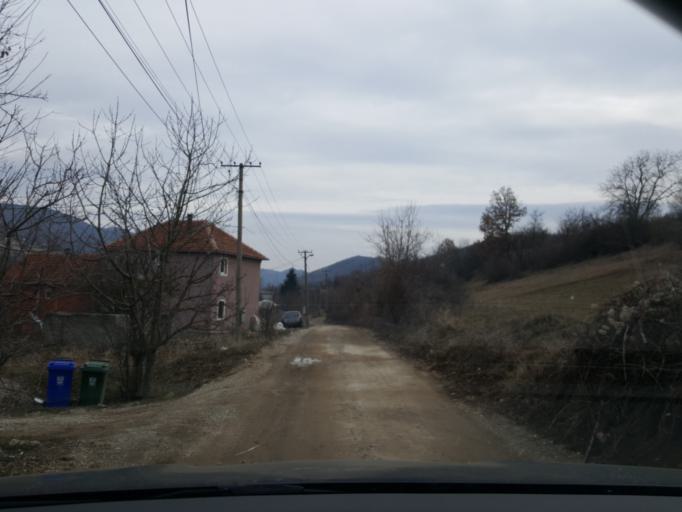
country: RS
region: Central Serbia
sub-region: Pirotski Okrug
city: Dimitrovgrad
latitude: 43.0078
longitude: 22.7541
